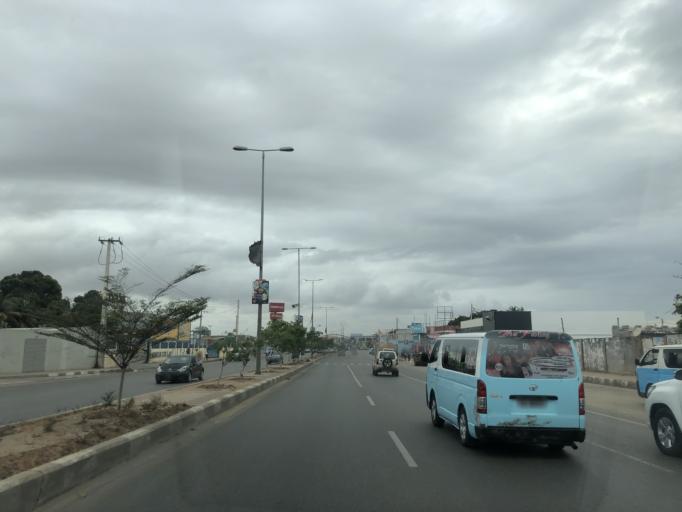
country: AO
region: Luanda
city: Luanda
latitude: -8.8752
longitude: 13.2107
